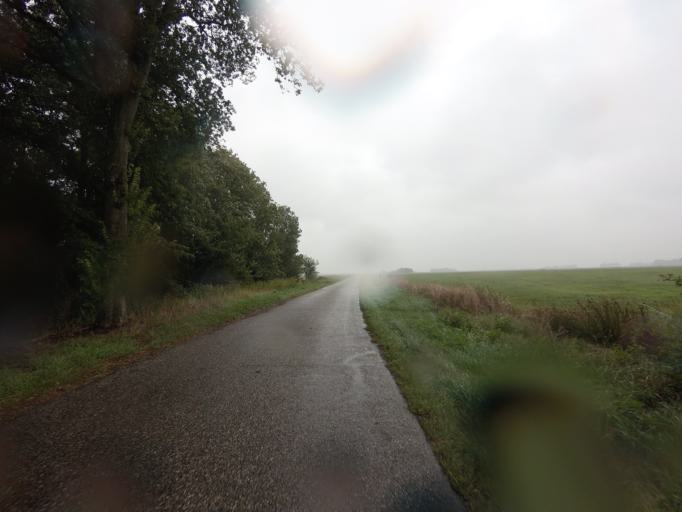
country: NL
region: Friesland
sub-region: Gemeente Boarnsterhim
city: Aldeboarn
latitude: 53.0748
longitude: 5.9288
